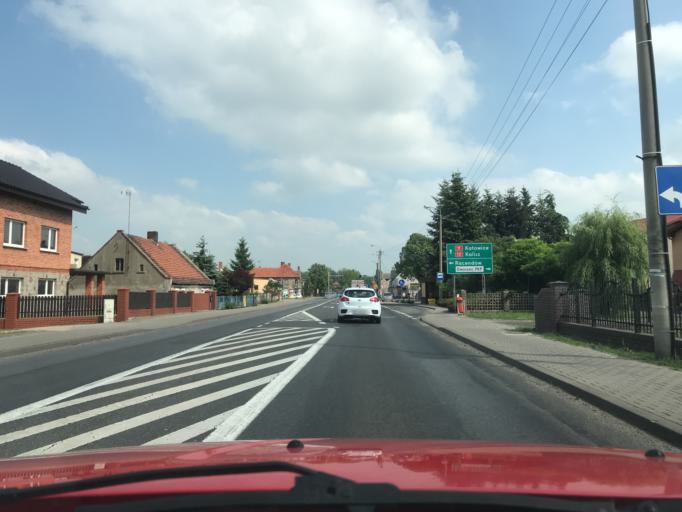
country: PL
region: Greater Poland Voivodeship
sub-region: Powiat jarocinski
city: Kotlin
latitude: 51.9194
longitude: 17.6458
